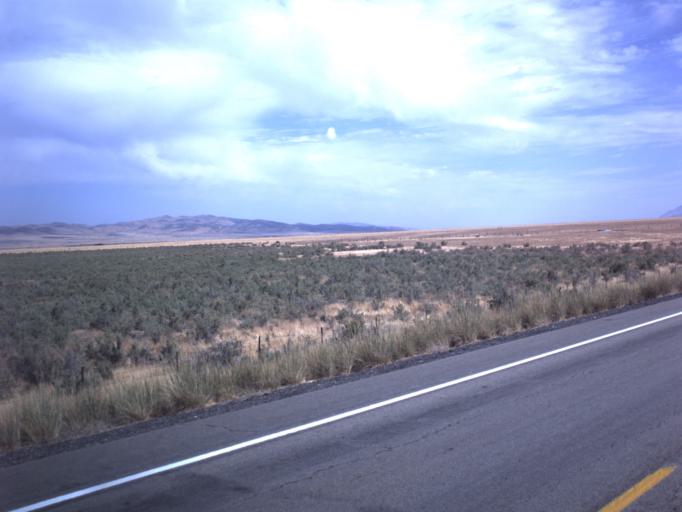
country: US
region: Utah
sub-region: Juab County
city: Nephi
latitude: 39.4856
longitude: -111.8860
